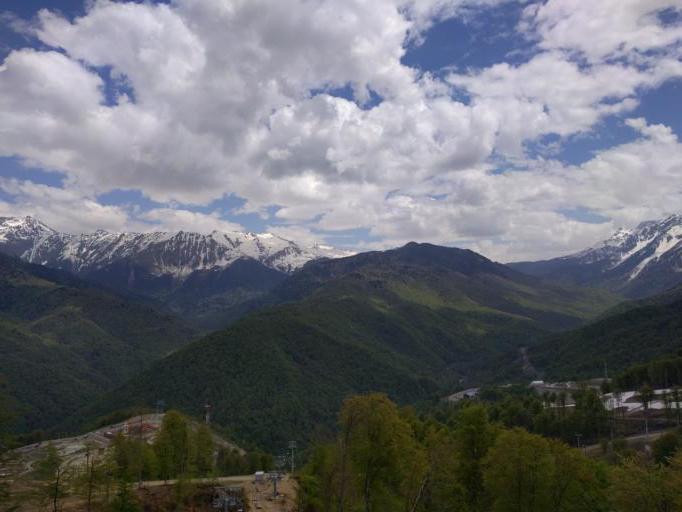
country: RU
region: Krasnodarskiy
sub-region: Sochi City
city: Krasnaya Polyana
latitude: 43.6531
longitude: 40.3179
